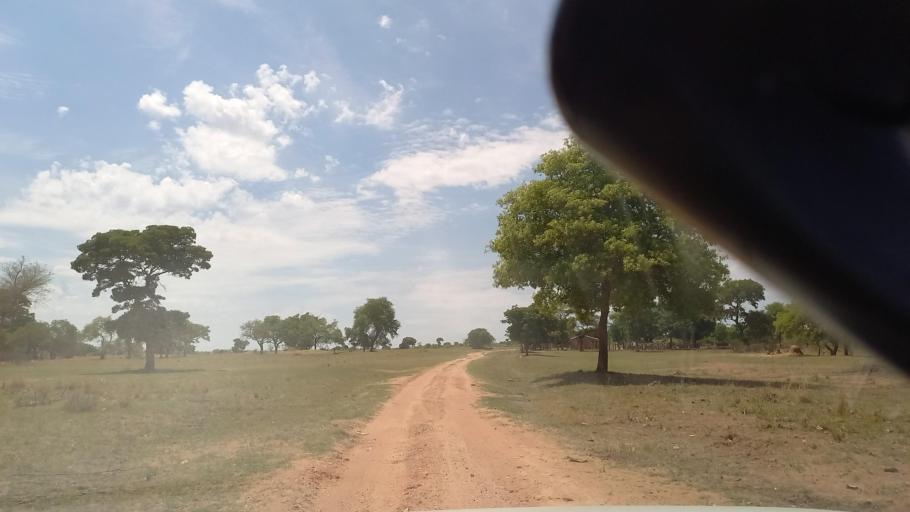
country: ZM
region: Southern
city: Mazabuka
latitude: -16.1504
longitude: 27.7785
